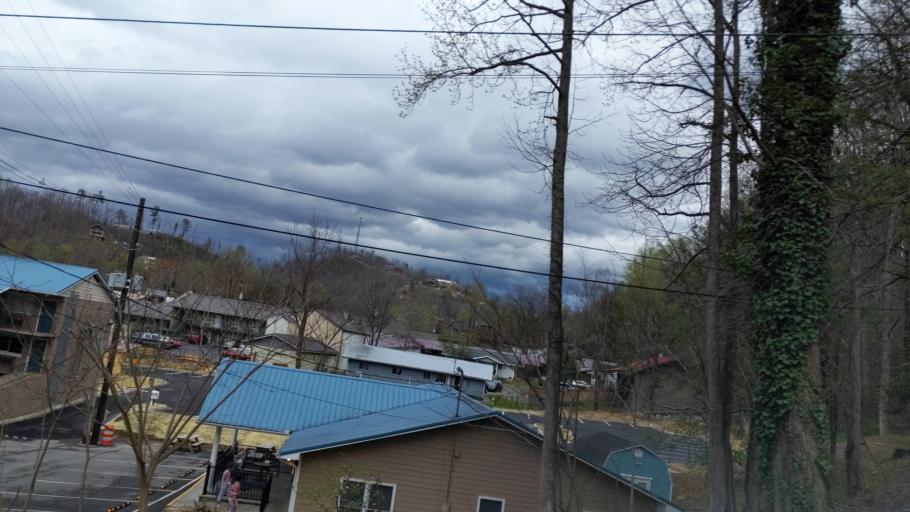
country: US
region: Tennessee
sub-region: Sevier County
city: Gatlinburg
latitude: 35.7151
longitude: -83.5071
